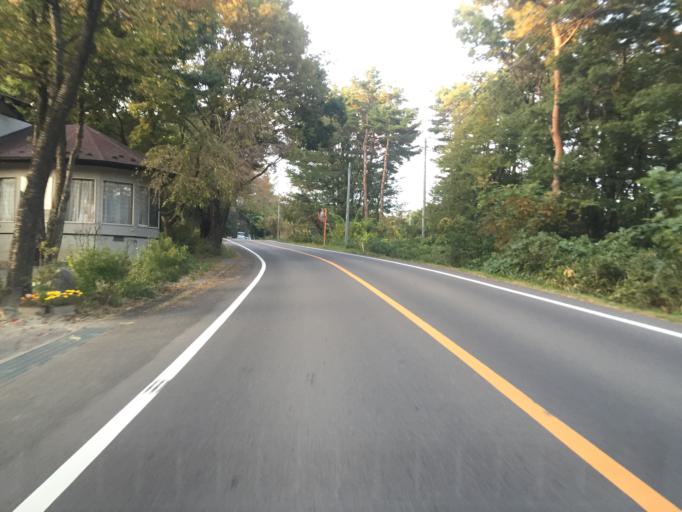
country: JP
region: Fukushima
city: Motomiya
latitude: 37.5762
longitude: 140.3519
